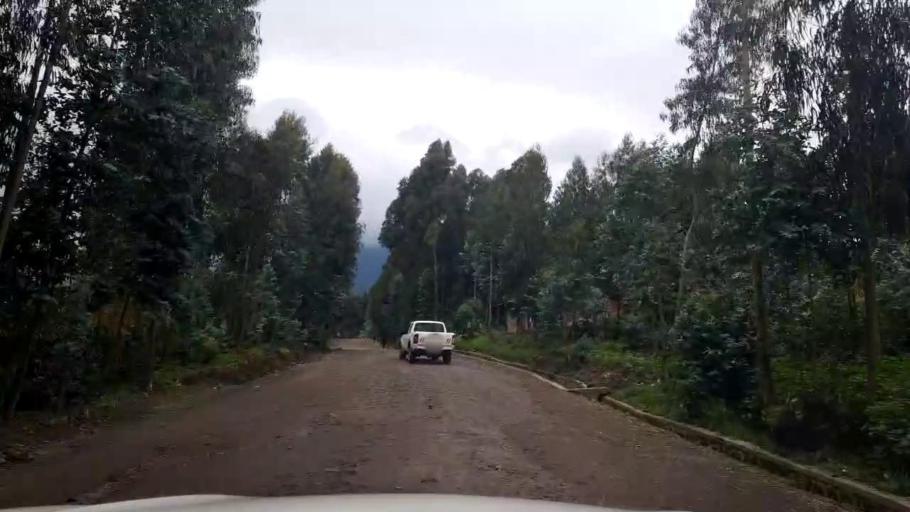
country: RW
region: Northern Province
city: Musanze
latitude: -1.4439
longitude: 29.5347
